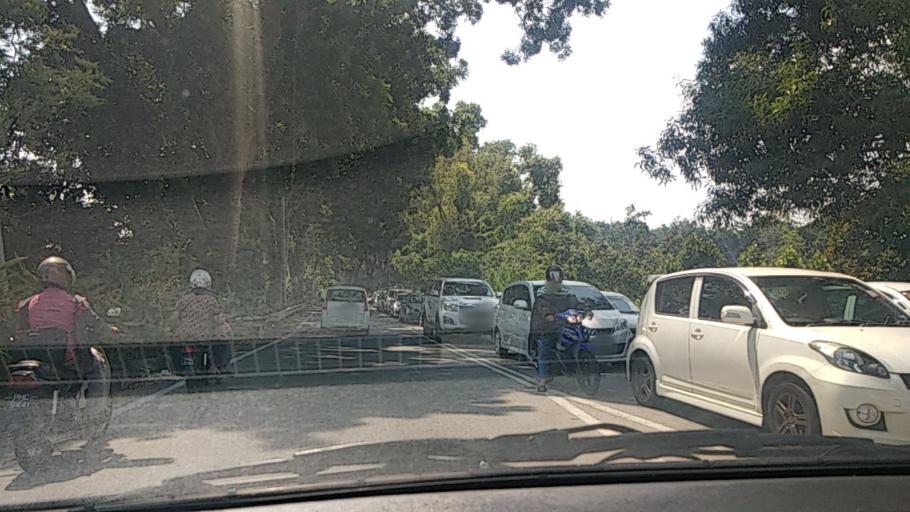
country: MY
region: Kedah
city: Sungai Petani
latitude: 5.6420
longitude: 100.5076
